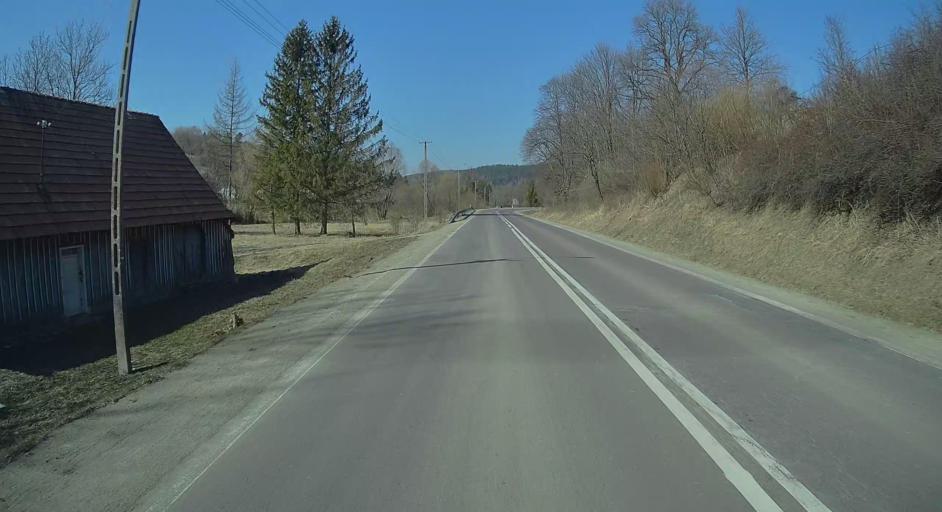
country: PL
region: Subcarpathian Voivodeship
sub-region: Powiat bieszczadzki
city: Ustrzyki Dolne
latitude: 49.5647
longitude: 22.5564
